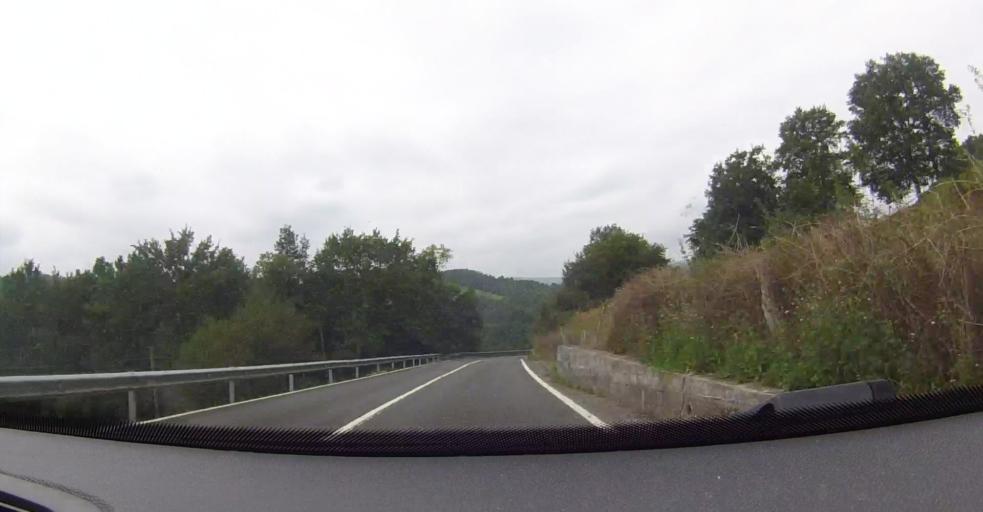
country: ES
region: Basque Country
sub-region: Bizkaia
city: Lanestosa
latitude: 43.2334
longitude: -3.3331
